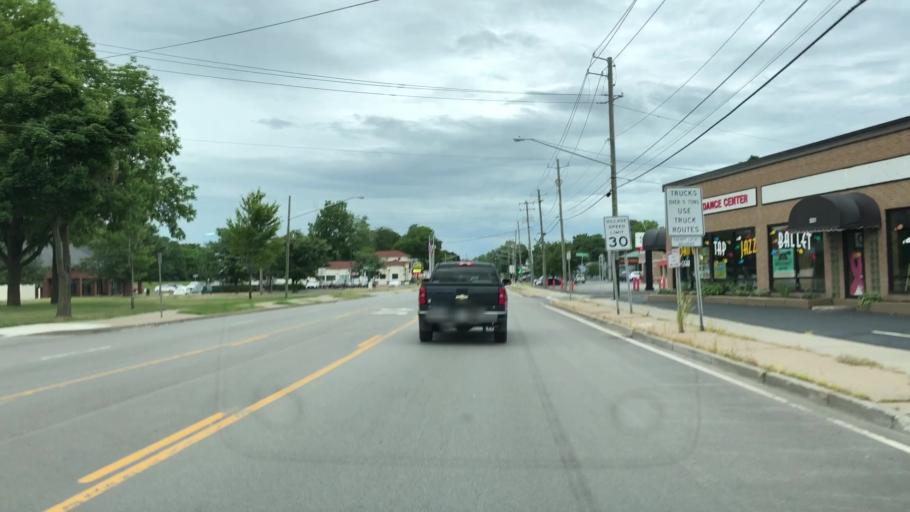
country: US
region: New York
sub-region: Erie County
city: Depew
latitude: 42.9011
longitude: -78.6823
